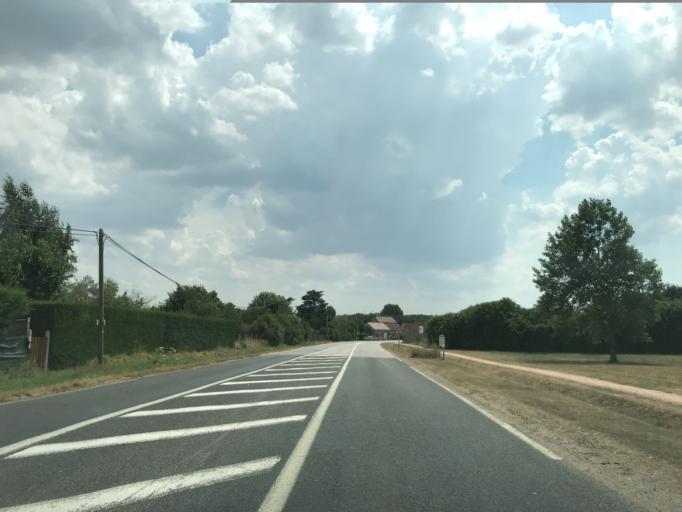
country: FR
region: Haute-Normandie
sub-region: Departement de l'Eure
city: Garennes-sur-Eure
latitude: 48.9150
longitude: 1.4447
